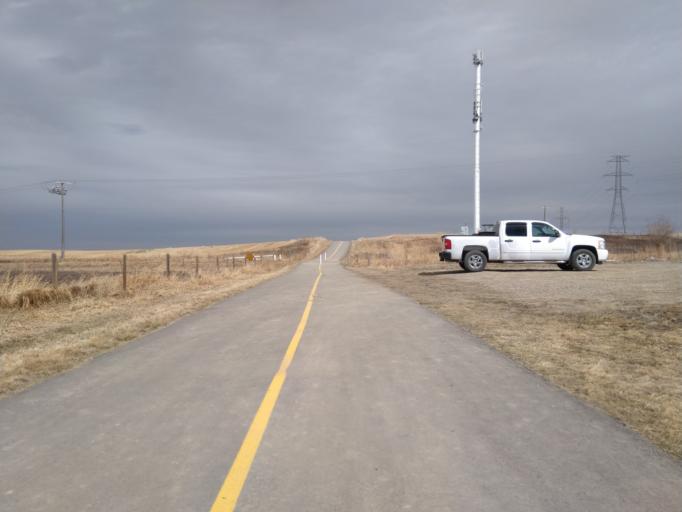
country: CA
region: Alberta
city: Airdrie
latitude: 51.1770
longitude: -114.0488
